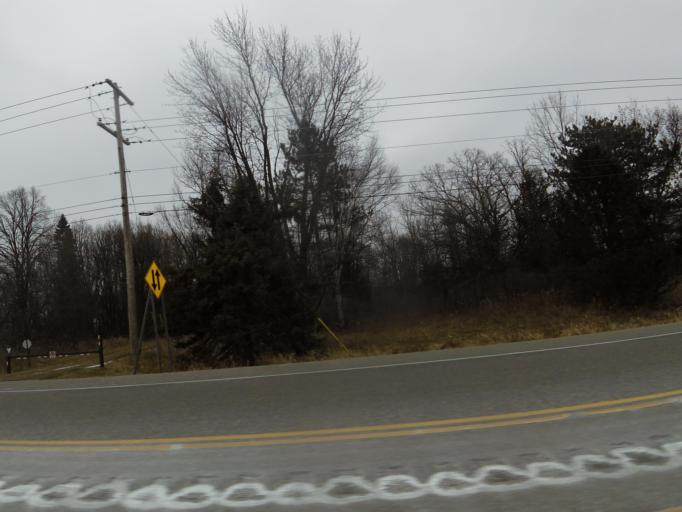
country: US
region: Minnesota
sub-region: Hennepin County
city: Maple Plain
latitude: 44.9970
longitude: -93.6268
